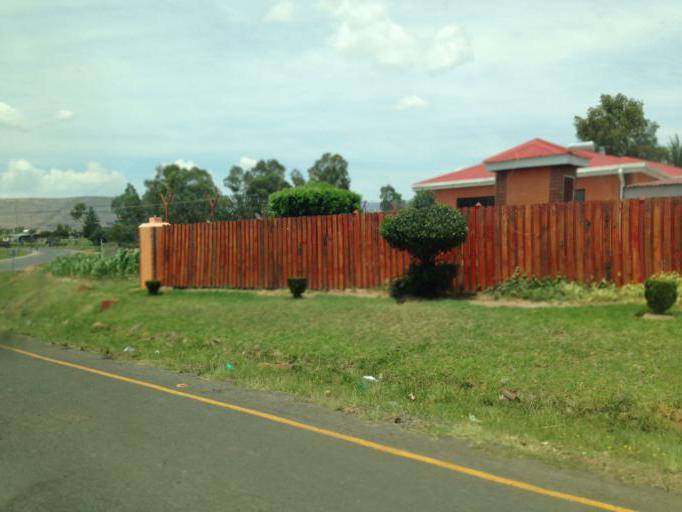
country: LS
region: Mafeteng
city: Mafeteng
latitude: -29.6915
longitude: 27.4380
